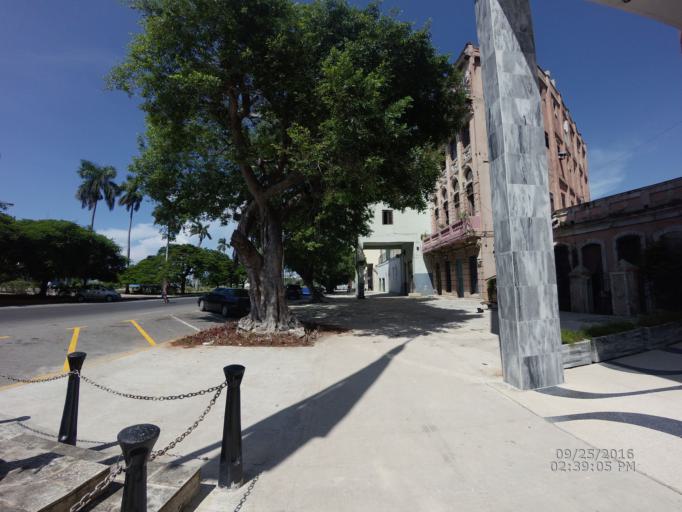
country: CU
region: La Habana
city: Centro Habana
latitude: 23.1425
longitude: -82.3559
